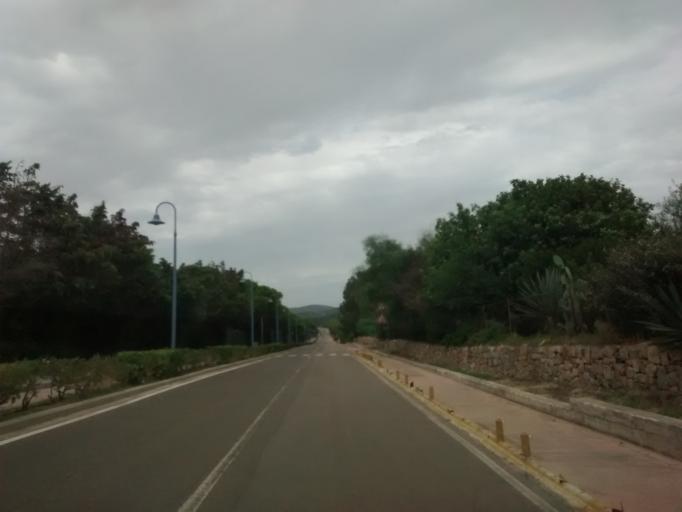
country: IT
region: Sardinia
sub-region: Provincia di Cagliari
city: Villasimius
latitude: 39.1207
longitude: 9.5110
